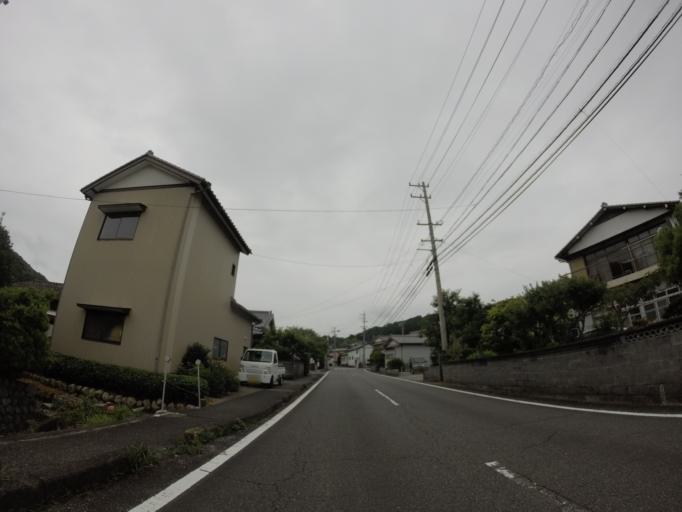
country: JP
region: Shizuoka
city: Shimada
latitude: 34.8059
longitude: 138.1803
